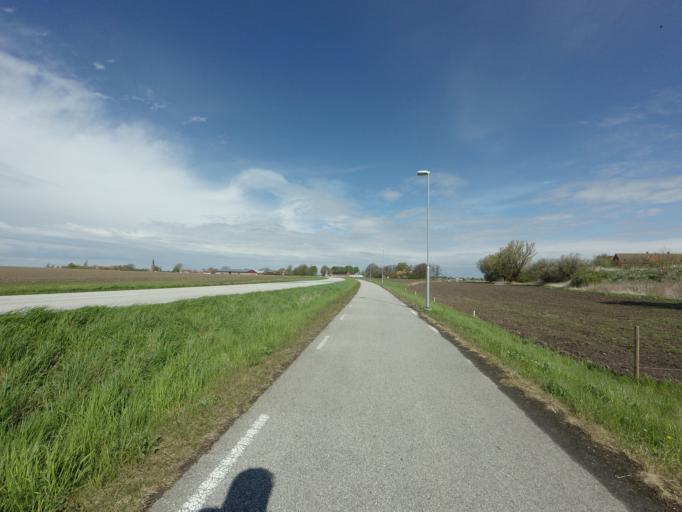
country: SE
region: Skane
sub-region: Malmo
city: Tygelsjo
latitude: 55.4978
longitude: 13.0000
